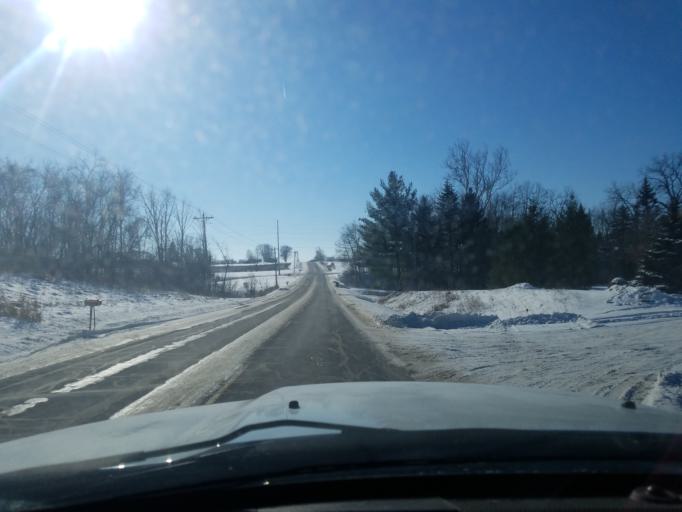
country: US
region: Indiana
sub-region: Noble County
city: Kendallville
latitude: 41.4255
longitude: -85.2326
